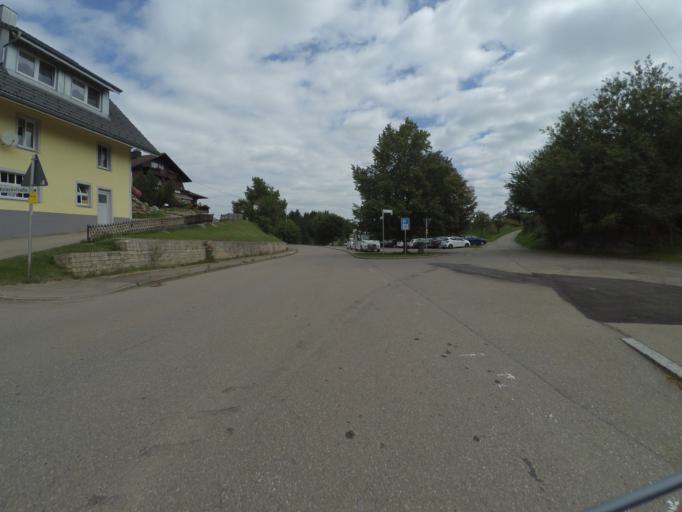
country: DE
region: Baden-Wuerttemberg
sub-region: Freiburg Region
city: Bonndorf im Schwarzwald
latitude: 47.8367
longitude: 8.3500
